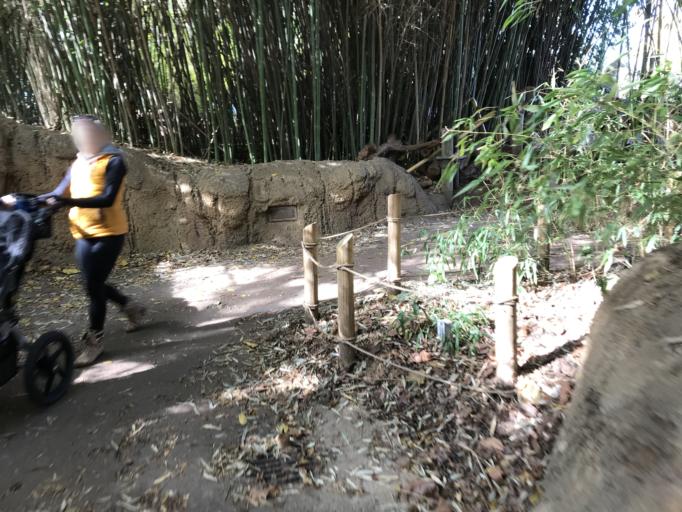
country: US
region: Kentucky
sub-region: Jefferson County
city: Audubon Park
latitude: 38.2068
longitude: -85.7022
